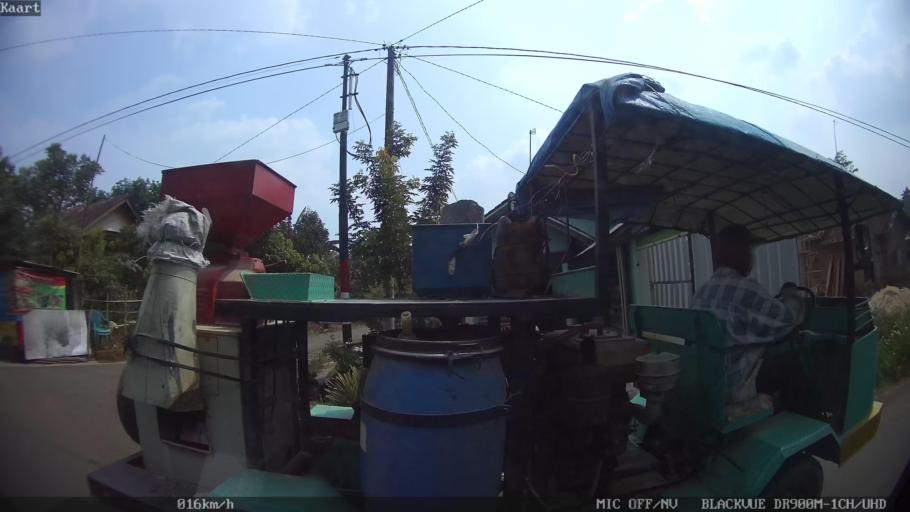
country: ID
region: Lampung
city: Gadingrejo
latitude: -5.3532
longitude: 105.0347
